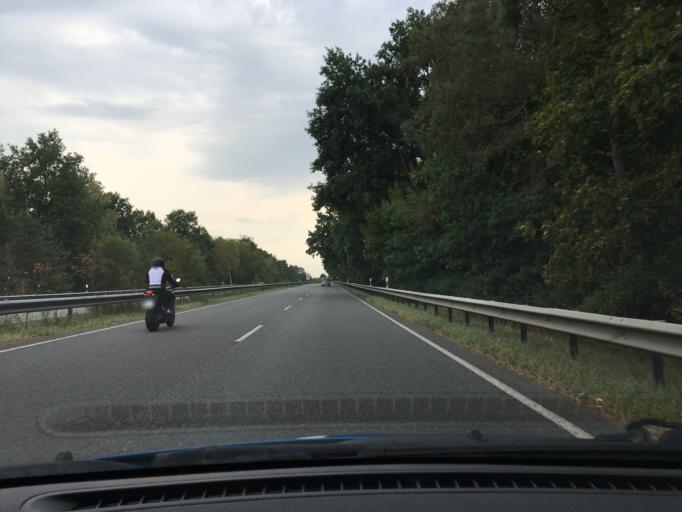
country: DE
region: Lower Saxony
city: Burgdorf
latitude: 52.5108
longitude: 10.0168
